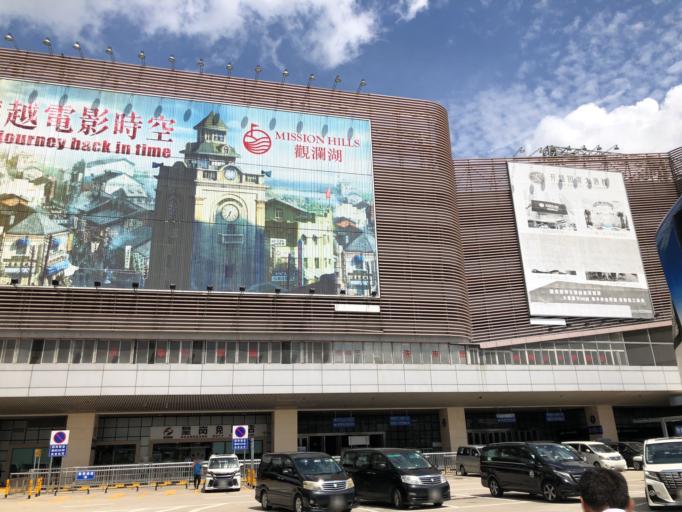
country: CN
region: Guangdong
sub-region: Shenzhen
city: Shenzhen
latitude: 22.5211
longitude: 114.0694
